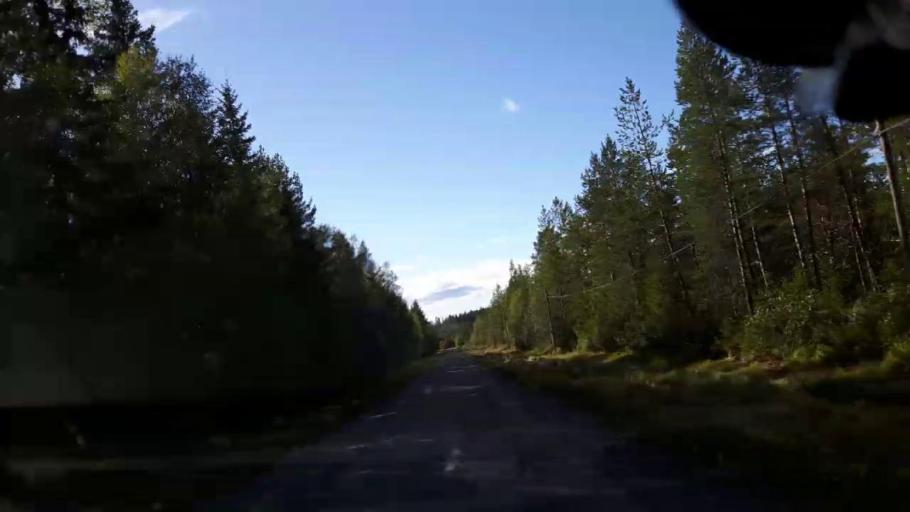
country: SE
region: Jaemtland
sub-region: Ragunda Kommun
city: Hammarstrand
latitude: 63.4801
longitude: 16.1367
